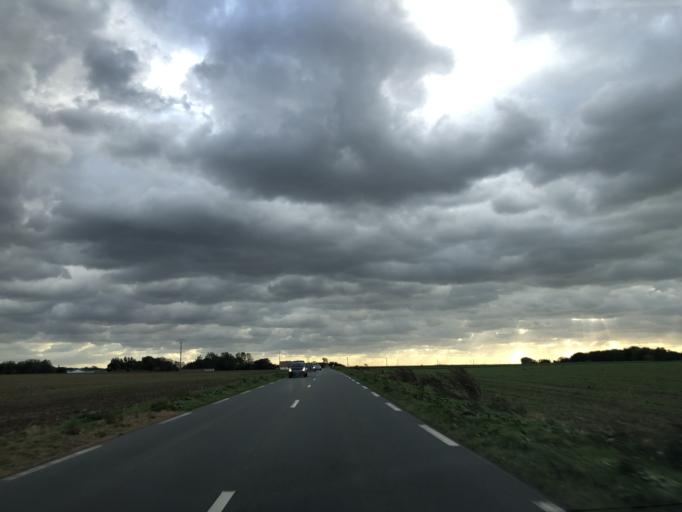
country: FR
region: Picardie
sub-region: Departement de la Somme
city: Ault
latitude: 50.0835
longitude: 1.4447
